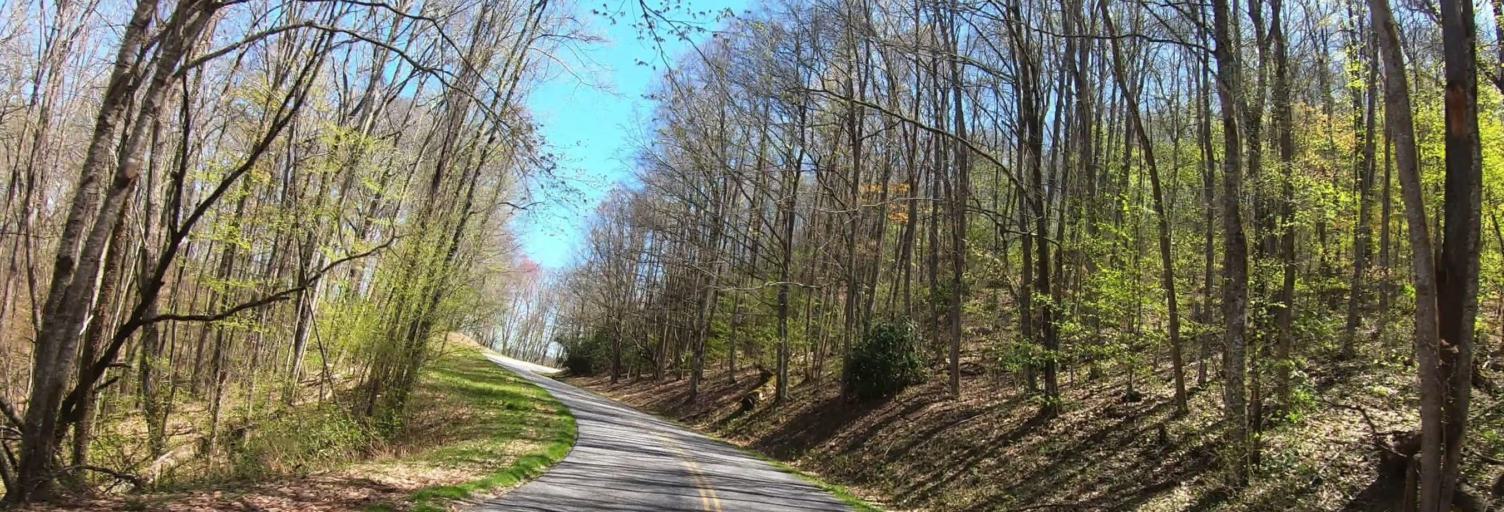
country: US
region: North Carolina
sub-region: Swain County
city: Cherokee
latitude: 35.5270
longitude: -83.2388
